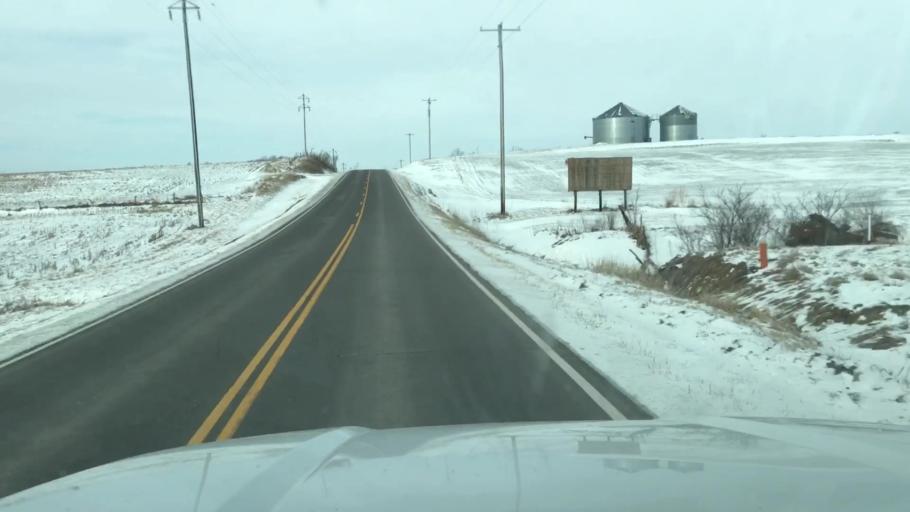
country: US
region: Missouri
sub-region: Holt County
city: Mound City
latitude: 40.1301
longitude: -95.0976
